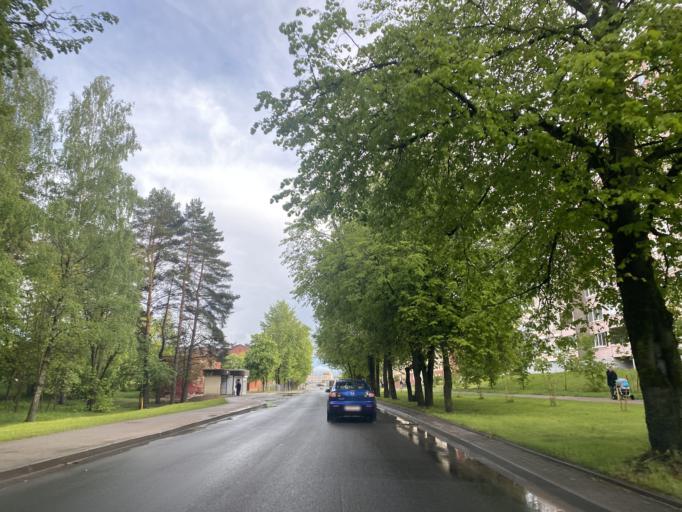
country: BY
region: Minsk
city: Borovlyany
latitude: 54.0020
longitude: 27.6835
